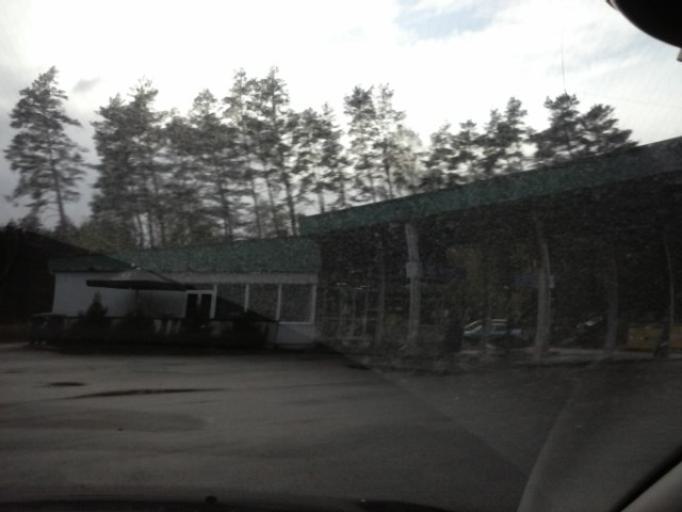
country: LV
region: Strenci
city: Strenci
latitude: 57.6255
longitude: 25.6722
